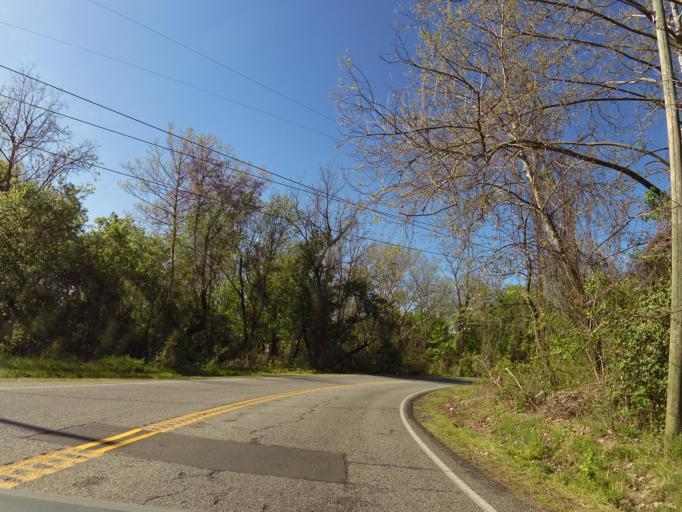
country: US
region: North Carolina
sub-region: Buncombe County
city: Asheville
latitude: 35.5643
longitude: -82.5638
